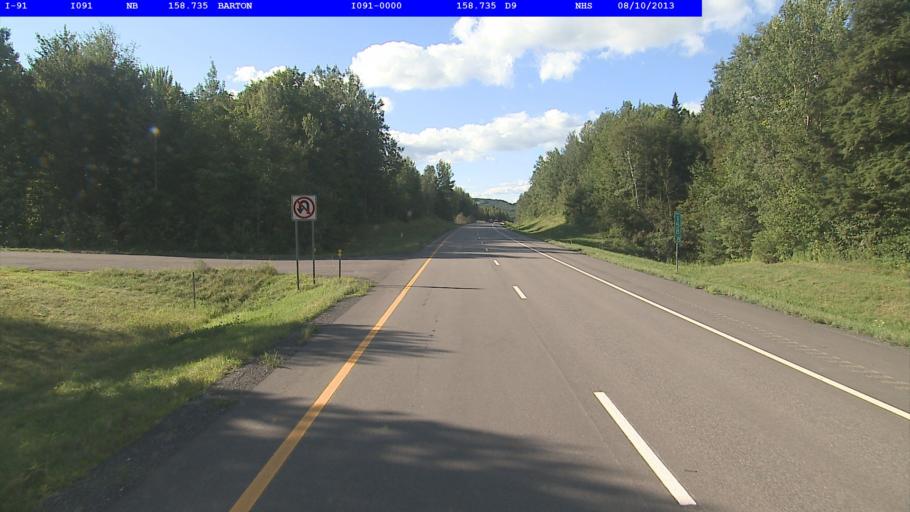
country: US
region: Vermont
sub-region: Orleans County
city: Newport
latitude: 44.7683
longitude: -72.2123
